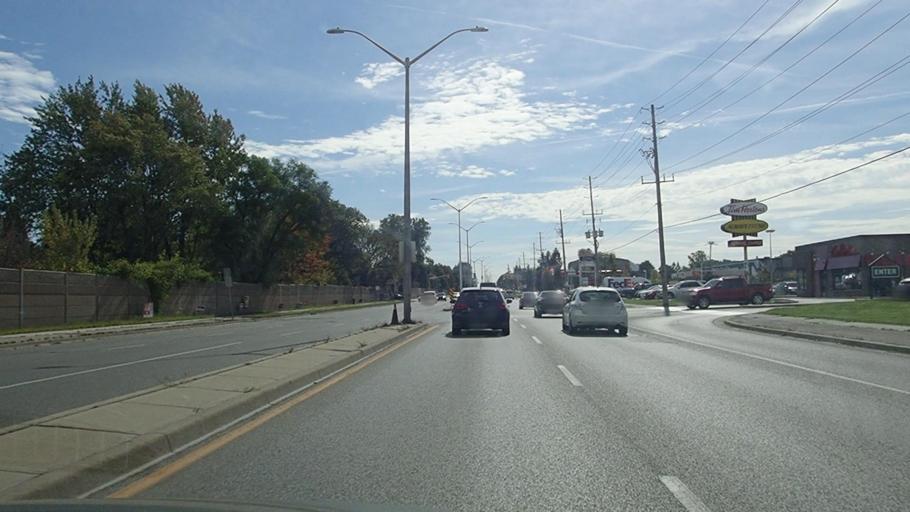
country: CA
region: Ontario
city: London
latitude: 43.0060
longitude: -81.3040
